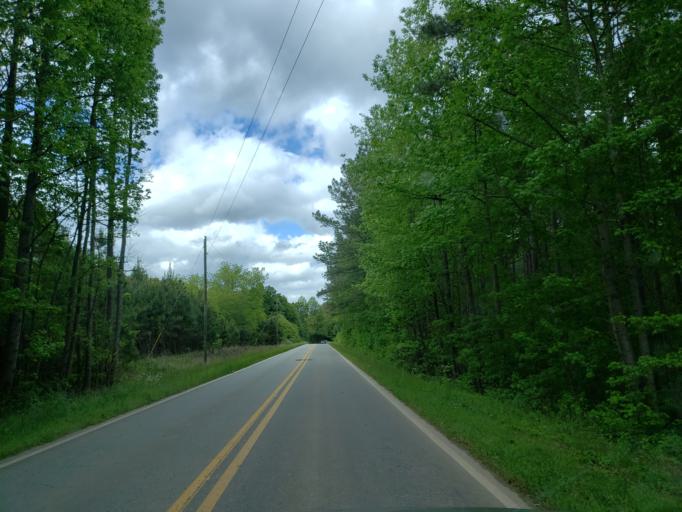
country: US
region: Georgia
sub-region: Haralson County
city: Tallapoosa
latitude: 33.6955
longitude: -85.3465
